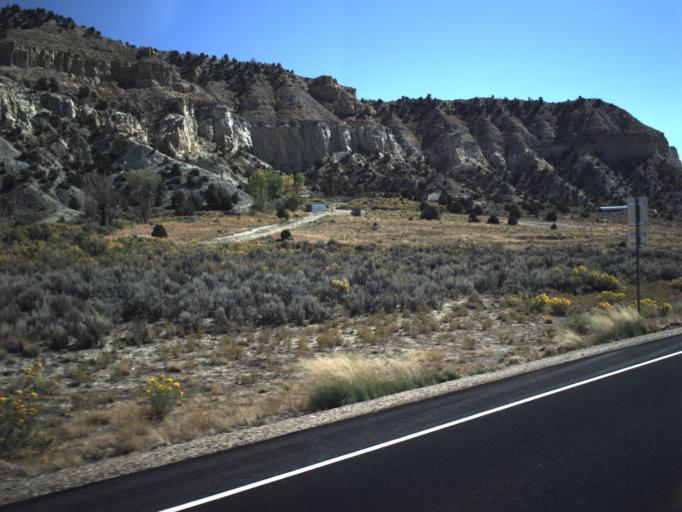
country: US
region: Utah
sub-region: Garfield County
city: Panguitch
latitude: 37.5679
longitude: -111.9900
